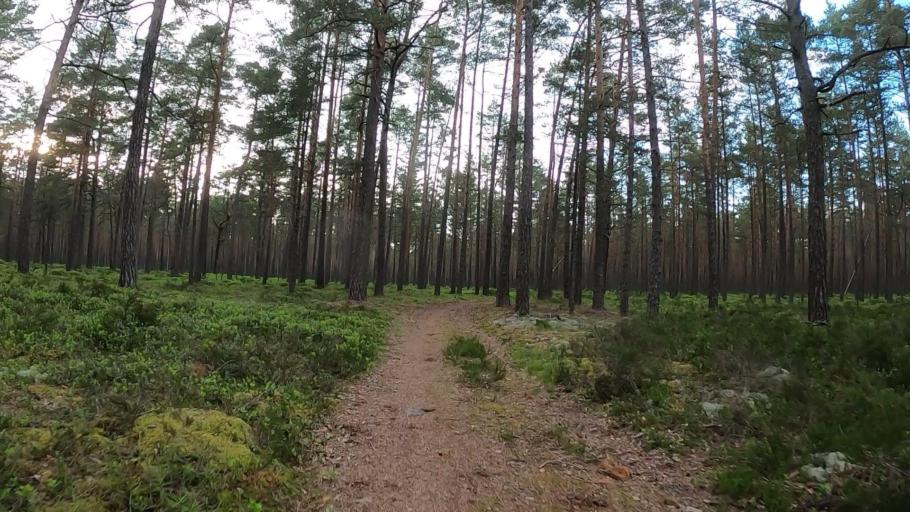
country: LV
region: Carnikava
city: Carnikava
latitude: 57.1599
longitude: 24.3035
